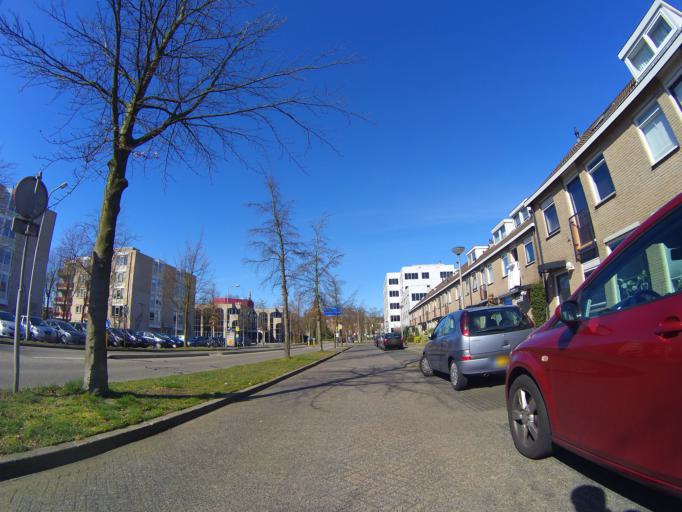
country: NL
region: Utrecht
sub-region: Gemeente Amersfoort
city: Randenbroek
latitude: 52.1532
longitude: 5.3956
